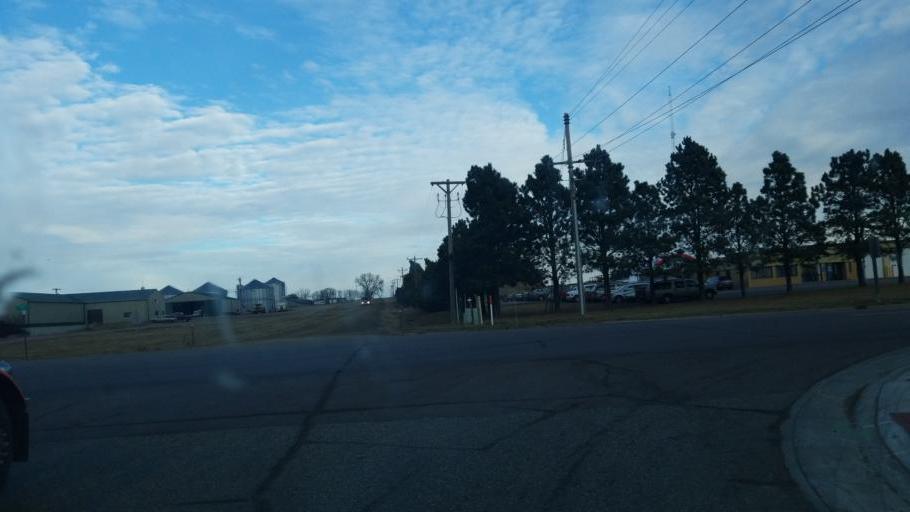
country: US
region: South Dakota
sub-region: Yankton County
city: Yankton
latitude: 42.9087
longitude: -97.4171
